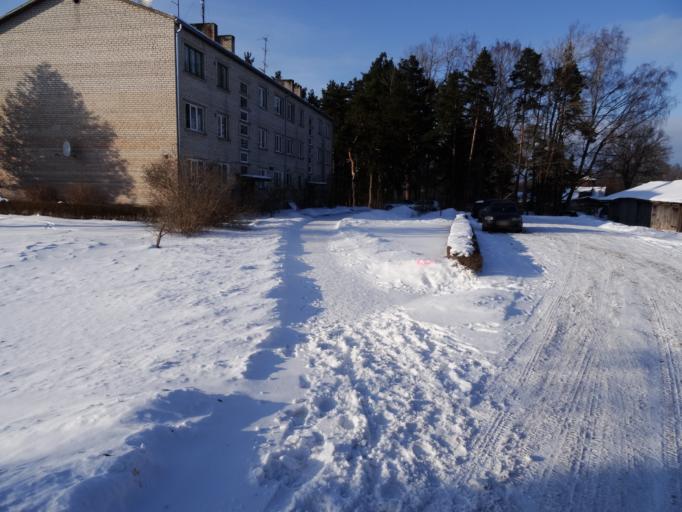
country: LV
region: Kuldigas Rajons
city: Kuldiga
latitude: 57.2787
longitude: 22.0151
